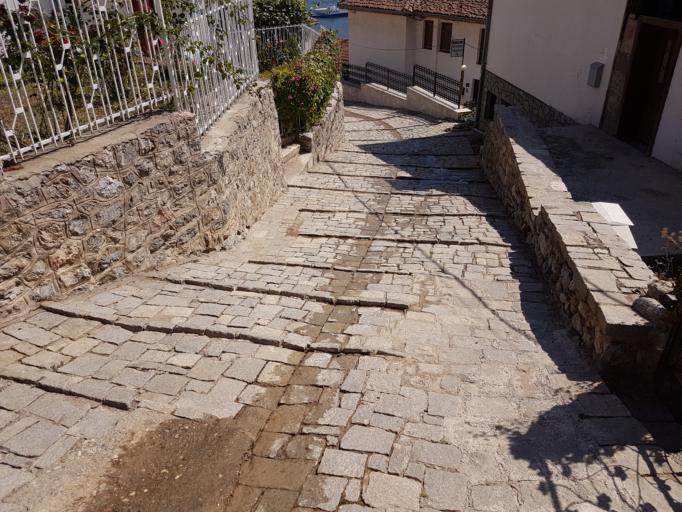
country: MK
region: Ohrid
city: Ohrid
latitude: 41.1129
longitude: 20.7959
